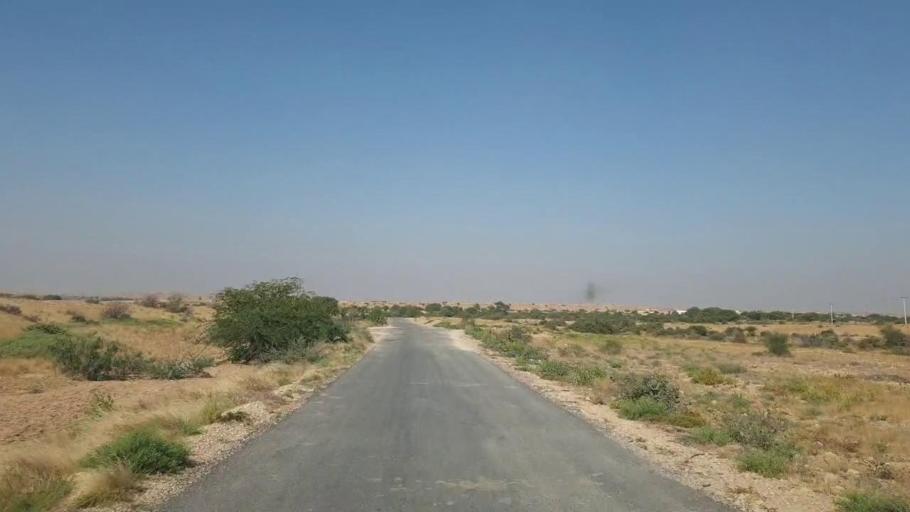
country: PK
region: Sindh
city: Thatta
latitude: 25.2101
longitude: 67.7973
